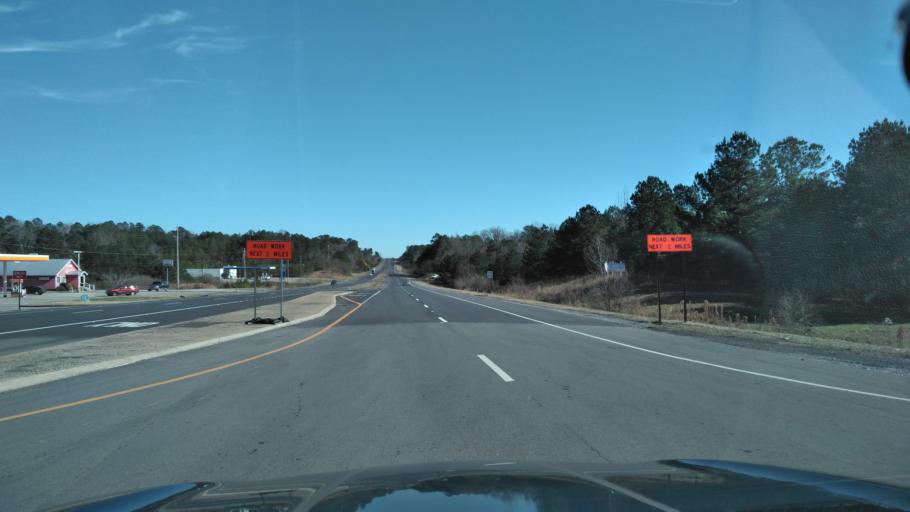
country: US
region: Alabama
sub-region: Walker County
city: Jasper
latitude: 33.8550
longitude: -87.3374
